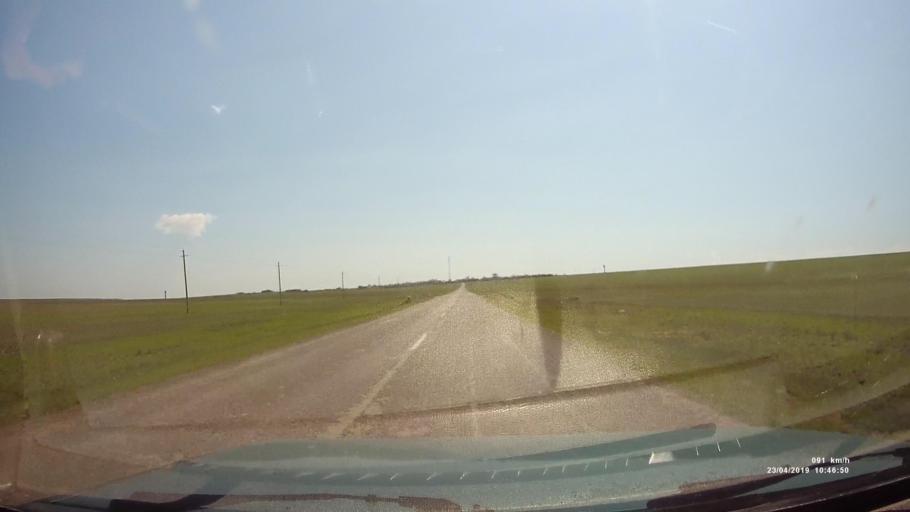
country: RU
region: Kalmykiya
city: Yashalta
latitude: 46.4397
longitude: 42.6975
